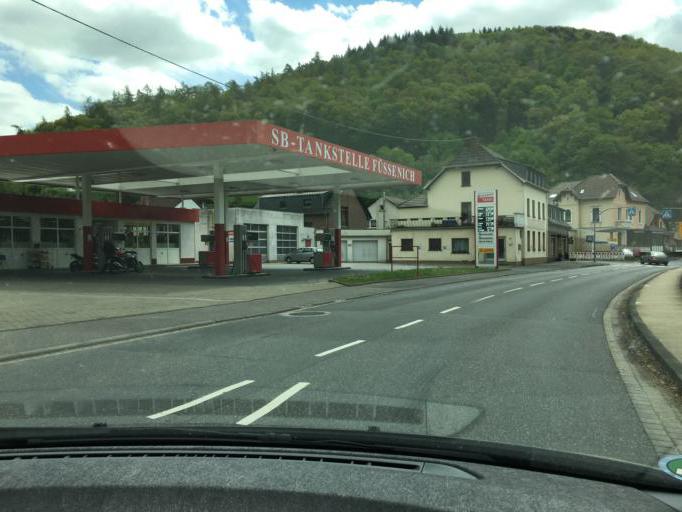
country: DE
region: Rheinland-Pfalz
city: Ahrbruck
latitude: 50.4860
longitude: 6.9736
